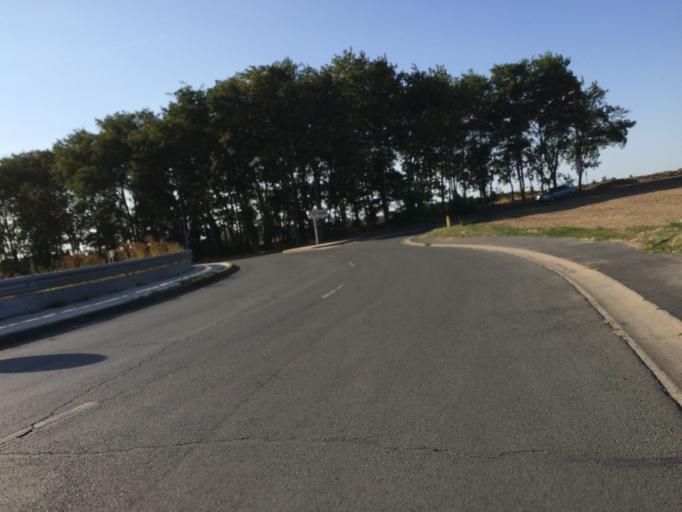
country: FR
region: Ile-de-France
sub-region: Departement de l'Essonne
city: Epinay-sur-Orge
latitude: 48.6706
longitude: 2.3098
